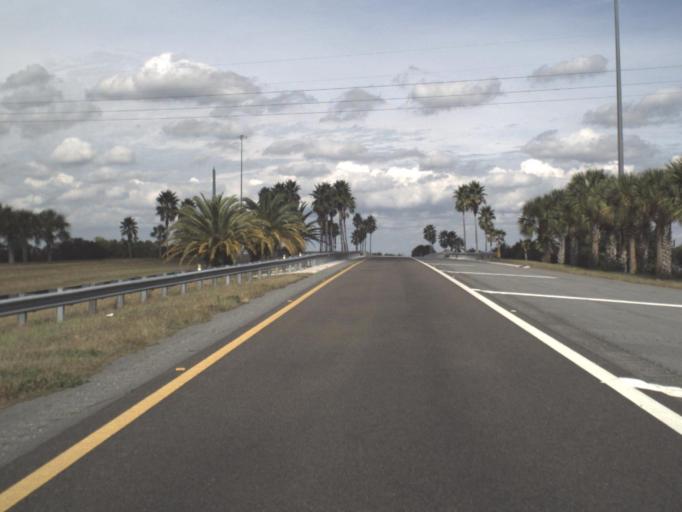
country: US
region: Florida
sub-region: Polk County
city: Polk City
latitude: 28.1527
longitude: -81.8459
